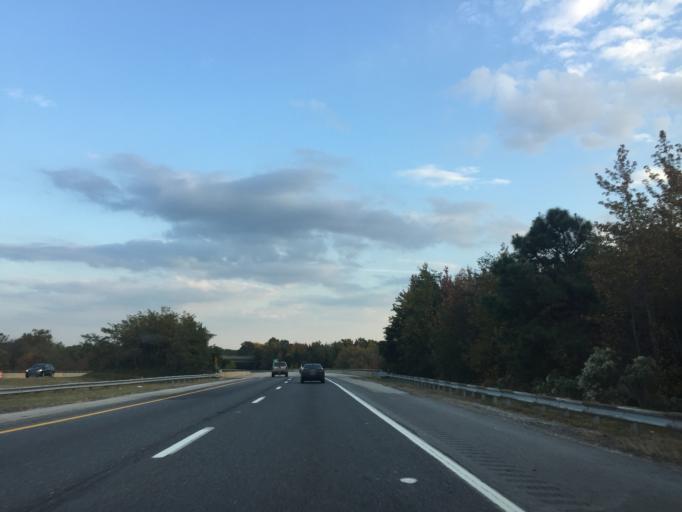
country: US
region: Maryland
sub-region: Baltimore County
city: Rossville
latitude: 39.3254
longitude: -76.4808
